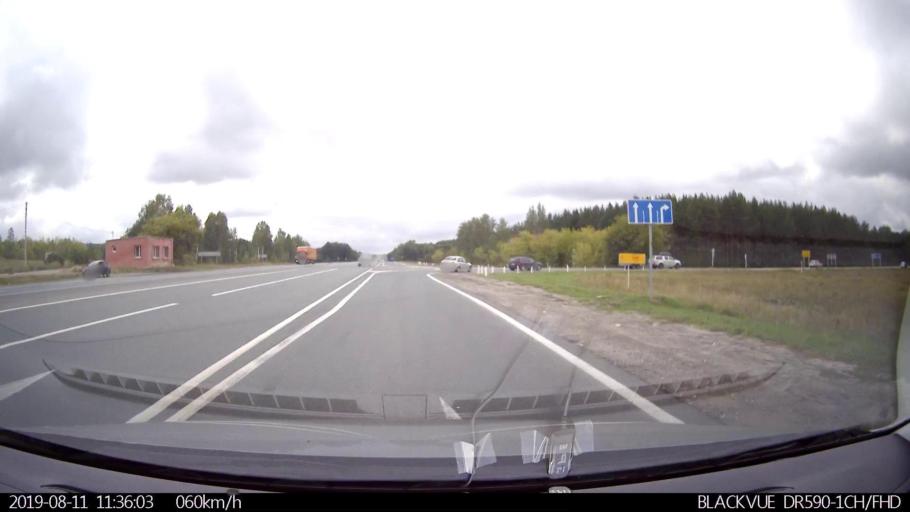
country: RU
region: Ulyanovsk
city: Silikatnyy
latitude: 54.0002
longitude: 48.2236
